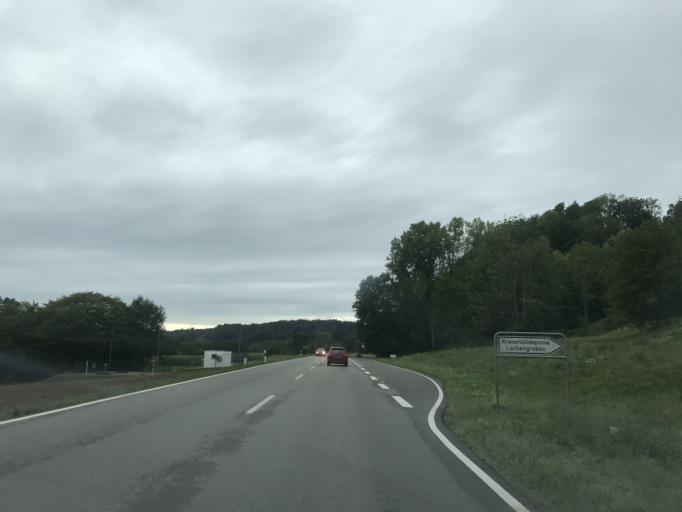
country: DE
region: Baden-Wuerttemberg
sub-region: Freiburg Region
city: Schworstadt
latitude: 47.5879
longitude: 7.8994
